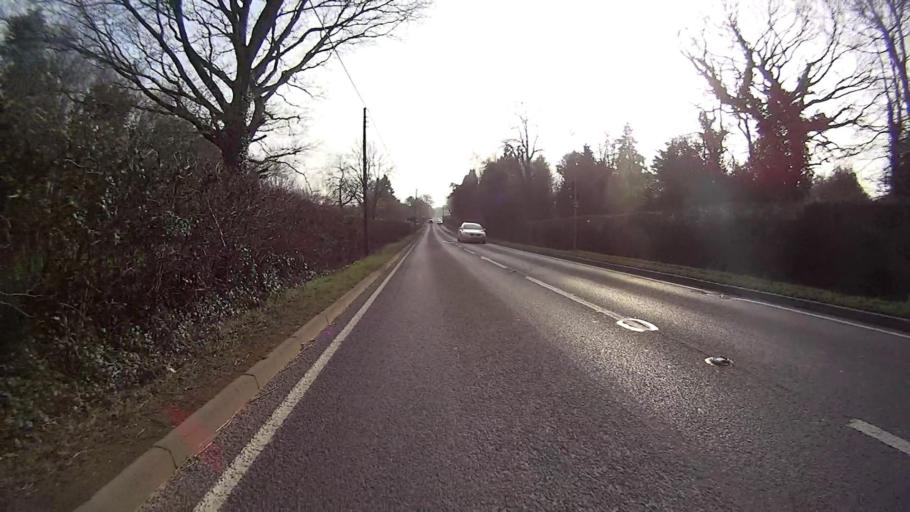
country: GB
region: England
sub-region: West Sussex
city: Crawley Down
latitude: 51.1167
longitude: -0.0851
